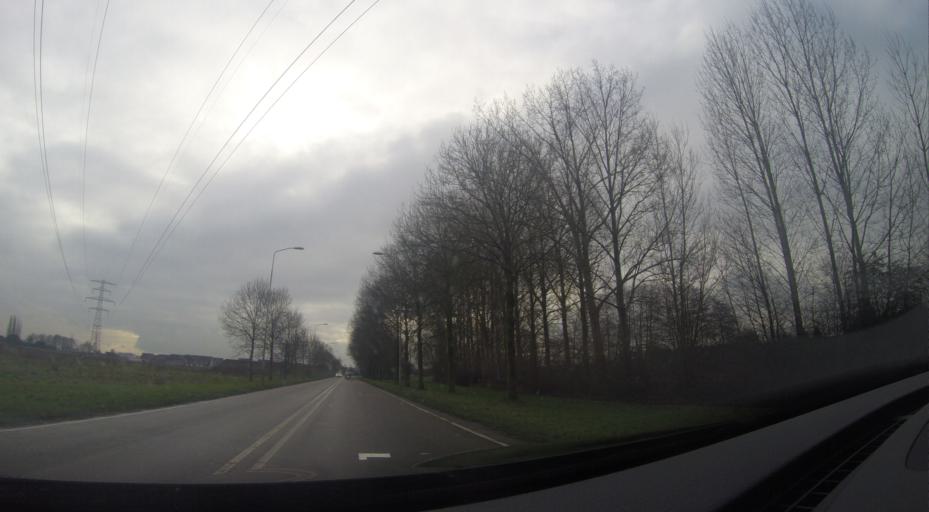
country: NL
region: Gelderland
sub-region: Gemeente Doetinchem
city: Doetinchem
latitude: 51.9558
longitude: 6.2752
